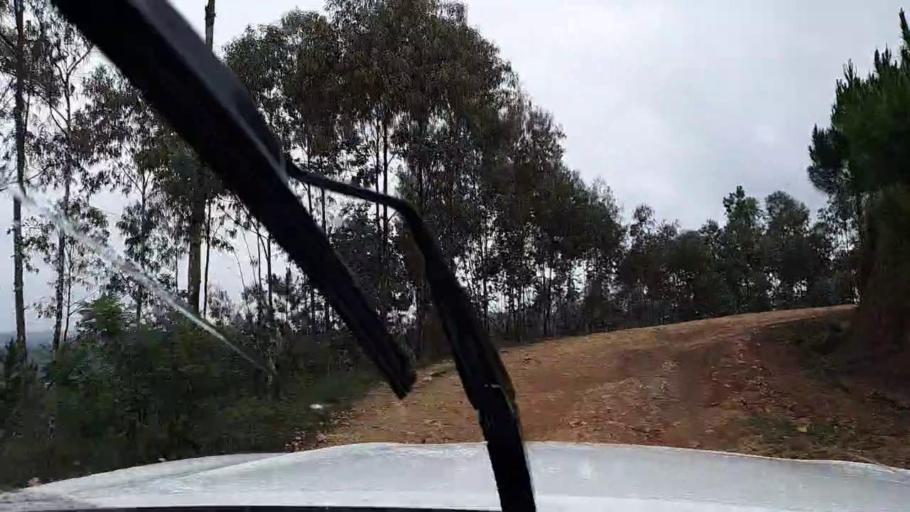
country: RW
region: Southern Province
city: Nzega
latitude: -2.4695
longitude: 29.4971
